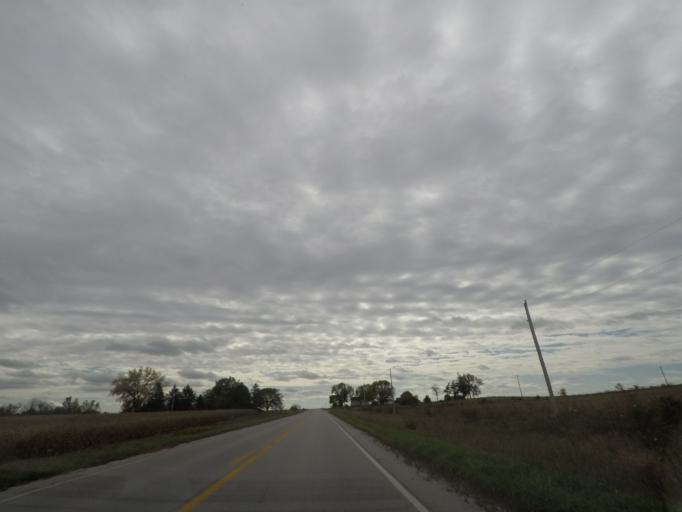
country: US
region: Iowa
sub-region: Story County
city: Huxley
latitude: 41.8646
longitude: -93.5317
